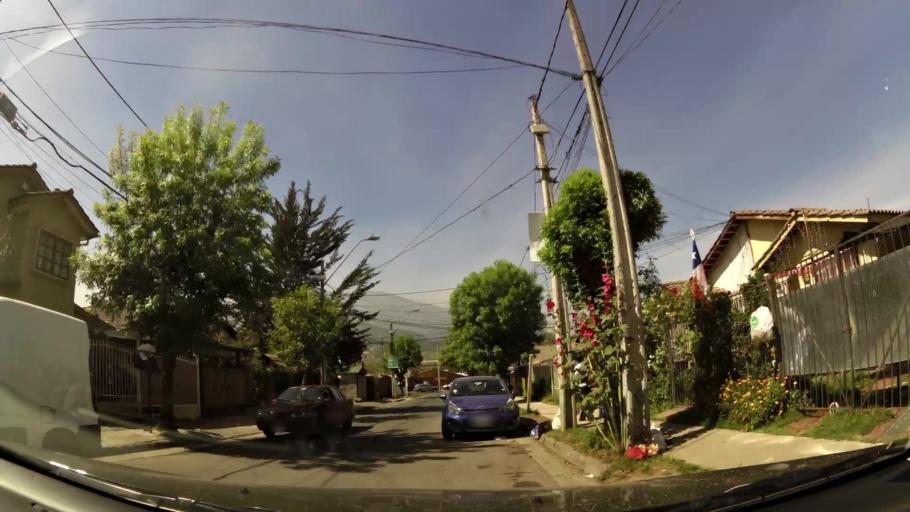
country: CL
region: Santiago Metropolitan
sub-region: Provincia de Cordillera
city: Puente Alto
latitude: -33.5738
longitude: -70.5614
